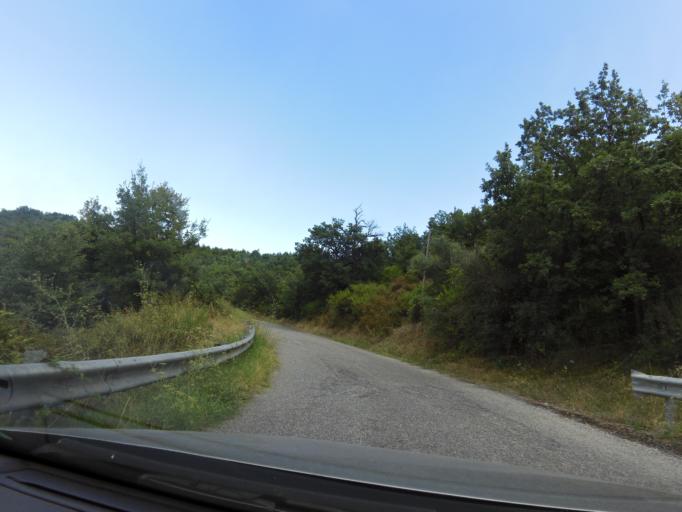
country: IT
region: Calabria
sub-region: Provincia di Reggio Calabria
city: Camini
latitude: 38.4340
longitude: 16.5058
